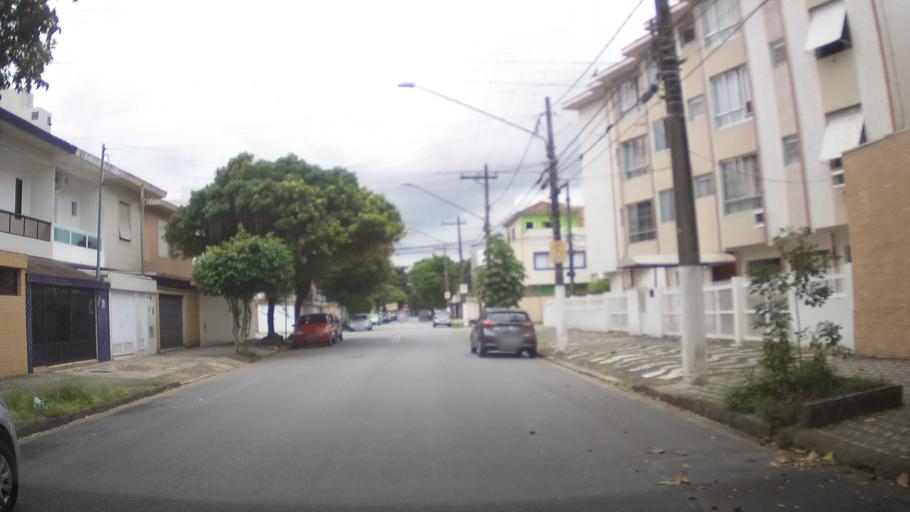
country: BR
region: Sao Paulo
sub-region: Santos
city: Santos
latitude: -23.9664
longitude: -46.3133
